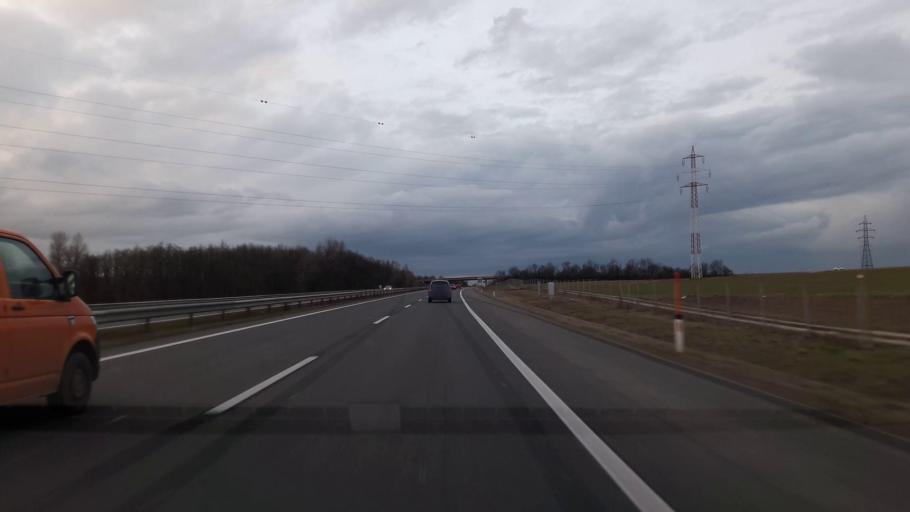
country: AT
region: Burgenland
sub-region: Eisenstadt-Umgebung
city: Steinbrunn
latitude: 47.8527
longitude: 16.4267
